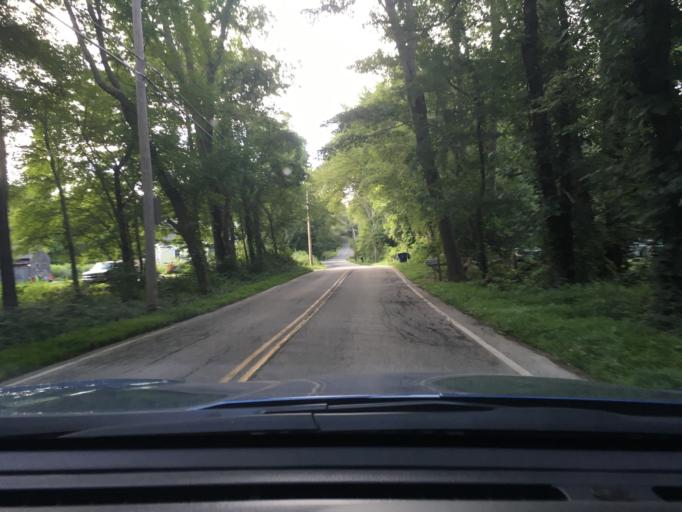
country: US
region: Rhode Island
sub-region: Washington County
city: Exeter
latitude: 41.6298
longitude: -71.5135
